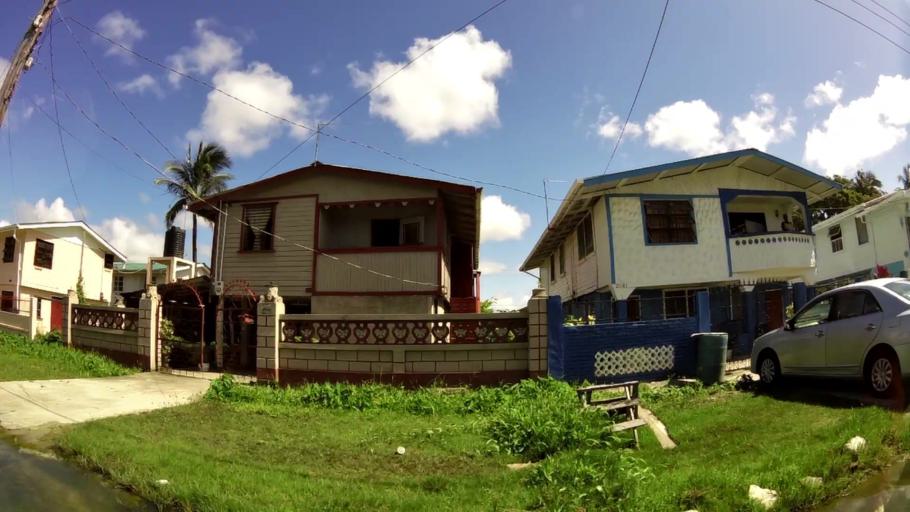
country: GY
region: Demerara-Mahaica
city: Georgetown
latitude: 6.7850
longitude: -58.1335
